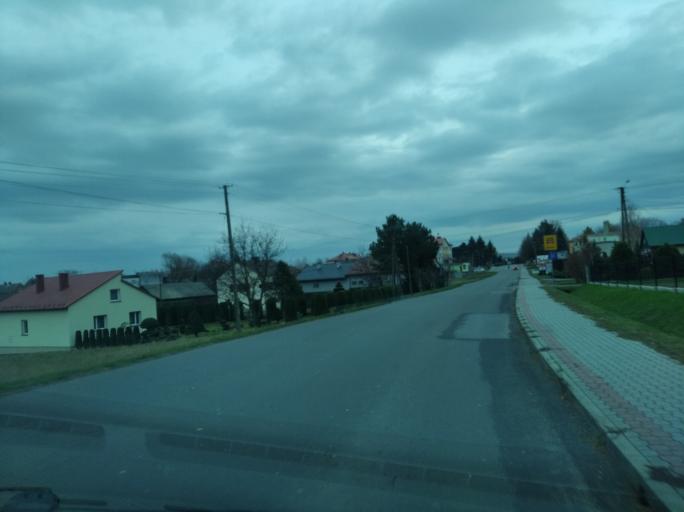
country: PL
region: Subcarpathian Voivodeship
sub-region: Powiat ropczycko-sedziszowski
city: Iwierzyce
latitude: 50.0301
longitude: 21.7550
